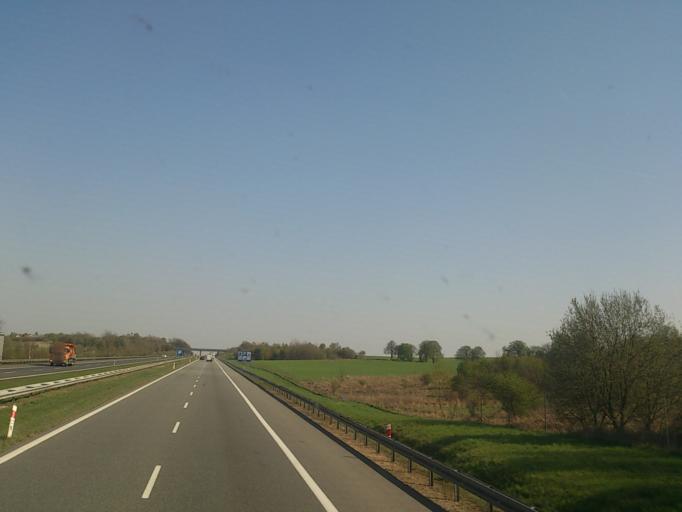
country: PL
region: Lesser Poland Voivodeship
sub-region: Powiat krakowski
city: Czulow
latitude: 50.0896
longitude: 19.6891
